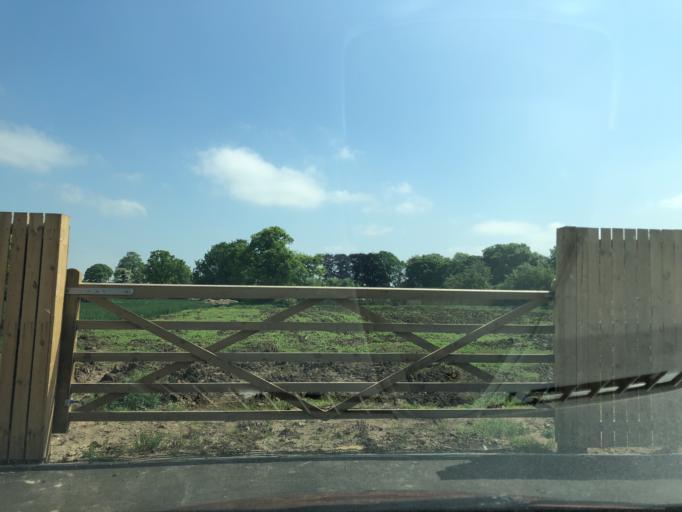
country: GB
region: England
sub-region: North Yorkshire
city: Bedale
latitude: 54.3037
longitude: -1.5574
